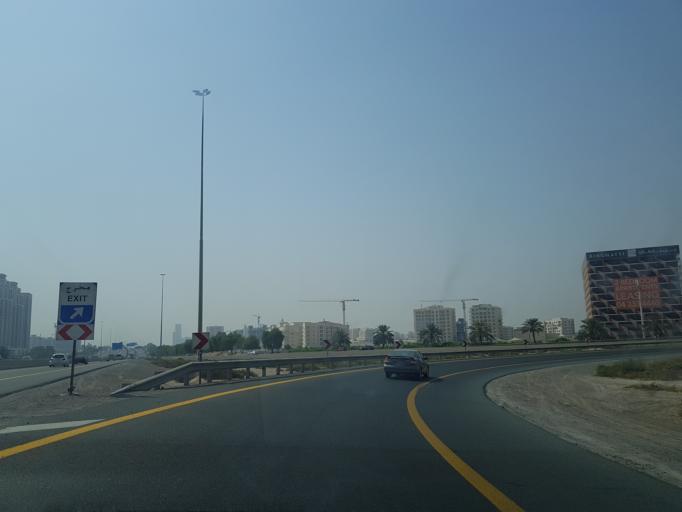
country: AE
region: Dubai
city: Dubai
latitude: 25.1189
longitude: 55.3651
